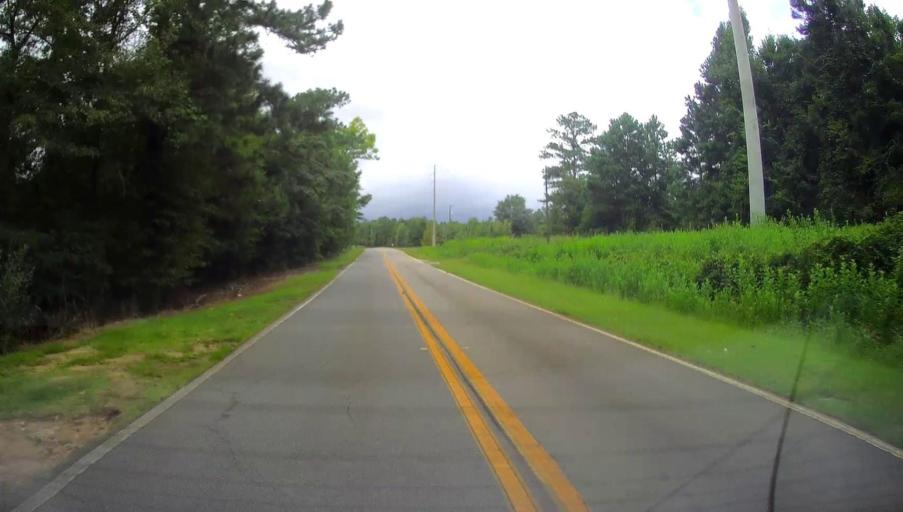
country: US
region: Georgia
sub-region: Bibb County
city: Macon
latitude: 32.7907
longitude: -83.5175
